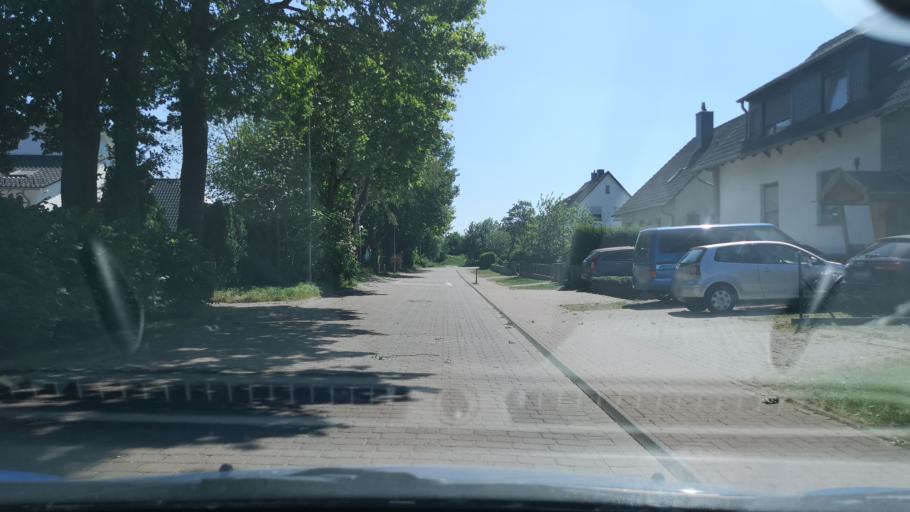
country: DE
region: Lower Saxony
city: Garbsen
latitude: 52.4544
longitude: 9.5614
